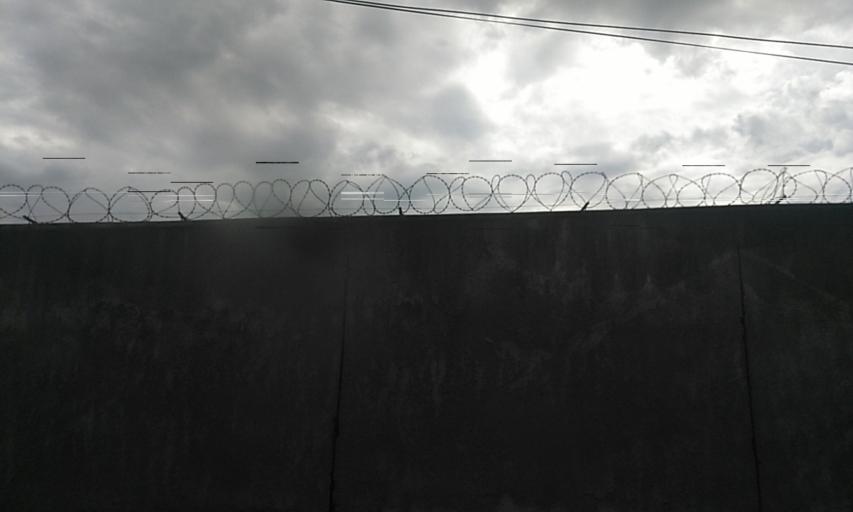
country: UG
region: Central Region
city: Kampala Central Division
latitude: 0.3387
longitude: 32.5899
